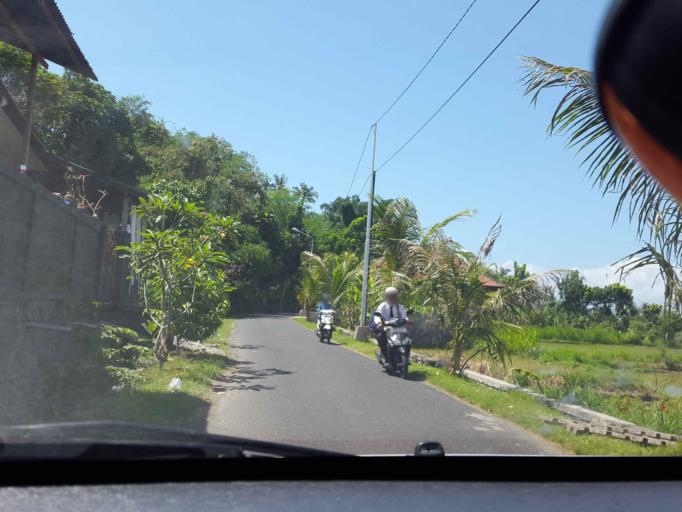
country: ID
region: Bali
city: Klungkung
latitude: -8.5343
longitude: 115.3919
